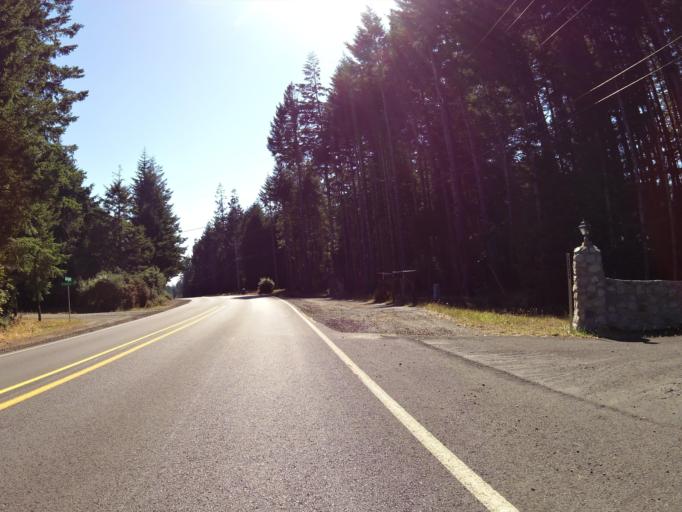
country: US
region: Oregon
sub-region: Coos County
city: Bandon
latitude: 43.1931
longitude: -124.3673
